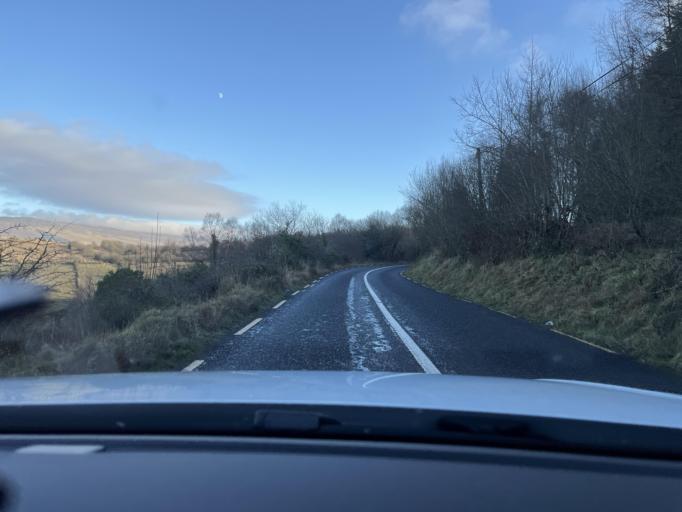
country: IE
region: Connaught
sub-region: County Leitrim
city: Manorhamilton
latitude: 54.2015
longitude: -7.9591
